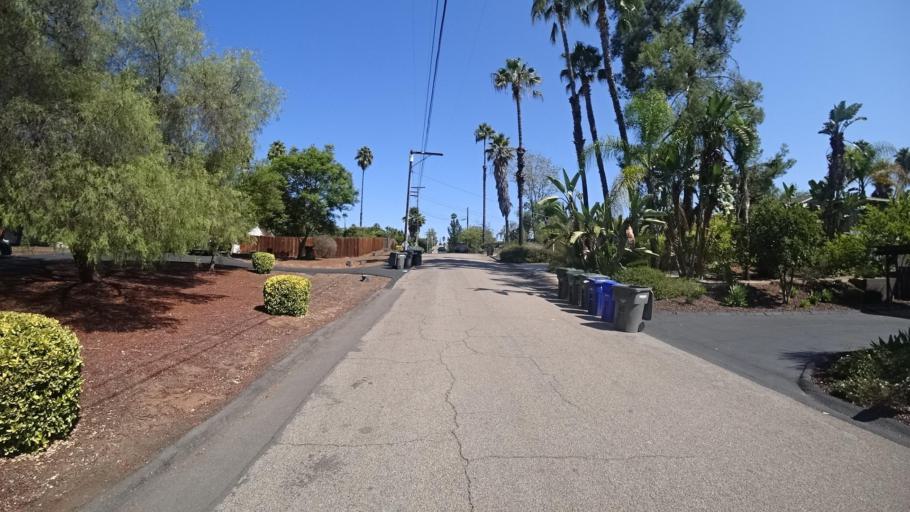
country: US
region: California
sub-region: San Diego County
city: Escondido
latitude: 33.0946
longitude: -117.0927
